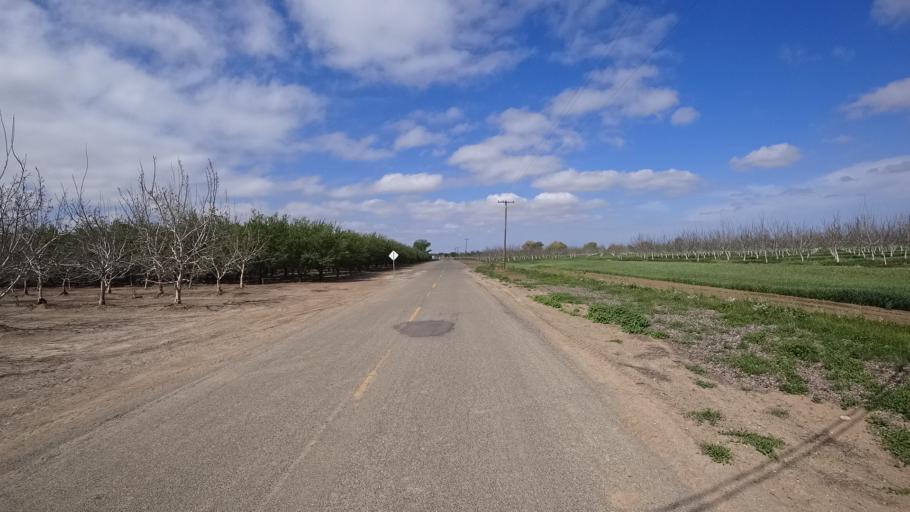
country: US
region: California
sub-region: Colusa County
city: Colusa
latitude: 39.4200
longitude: -121.9427
